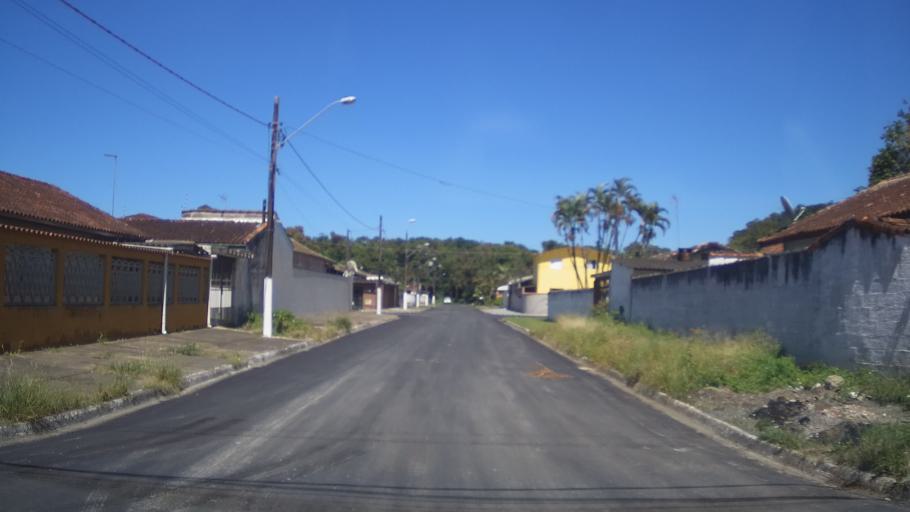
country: BR
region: Sao Paulo
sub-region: Mongagua
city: Mongagua
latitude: -24.0755
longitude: -46.5953
